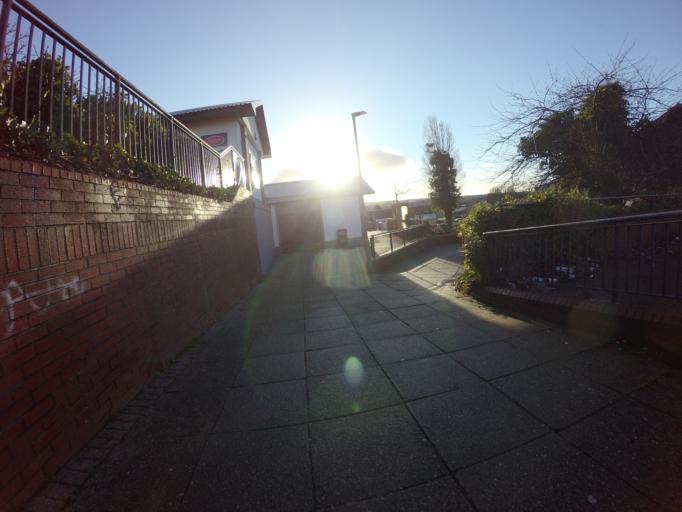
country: GB
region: Scotland
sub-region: West Lothian
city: Mid Calder
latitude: 55.8974
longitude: -3.4963
